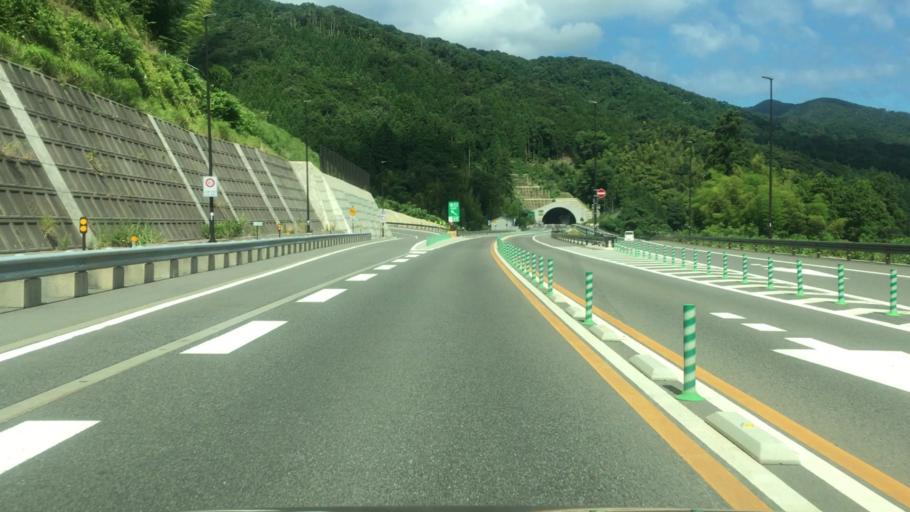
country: JP
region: Hyogo
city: Toyooka
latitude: 35.6377
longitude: 134.5676
